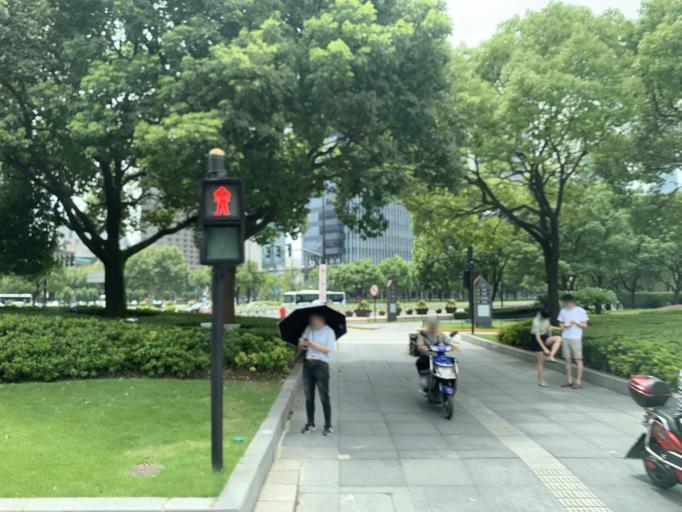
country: CN
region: Shanghai Shi
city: Pudong
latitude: 31.2326
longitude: 121.5205
